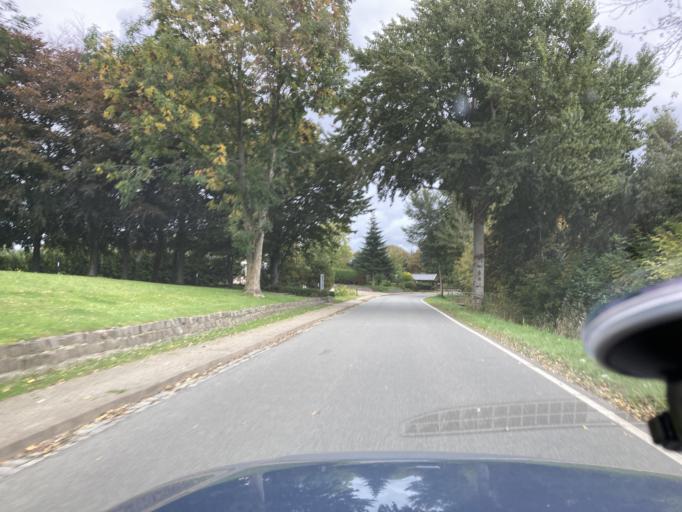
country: DE
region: Schleswig-Holstein
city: Reinsbuttel
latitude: 54.1777
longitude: 8.9147
